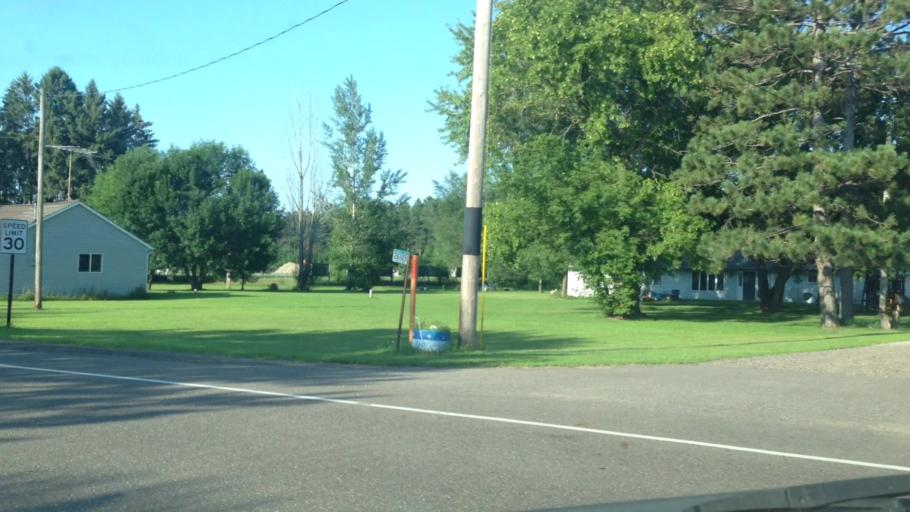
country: US
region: Minnesota
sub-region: Sherburne County
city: Big Lake
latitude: 45.4441
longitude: -93.7360
